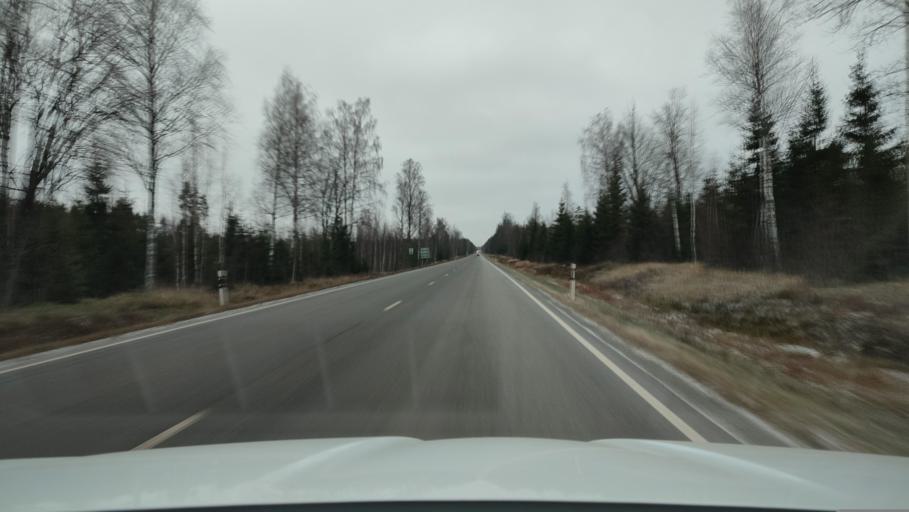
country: FI
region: Ostrobothnia
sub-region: Sydosterbotten
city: Naerpes
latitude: 62.5090
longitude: 21.4525
